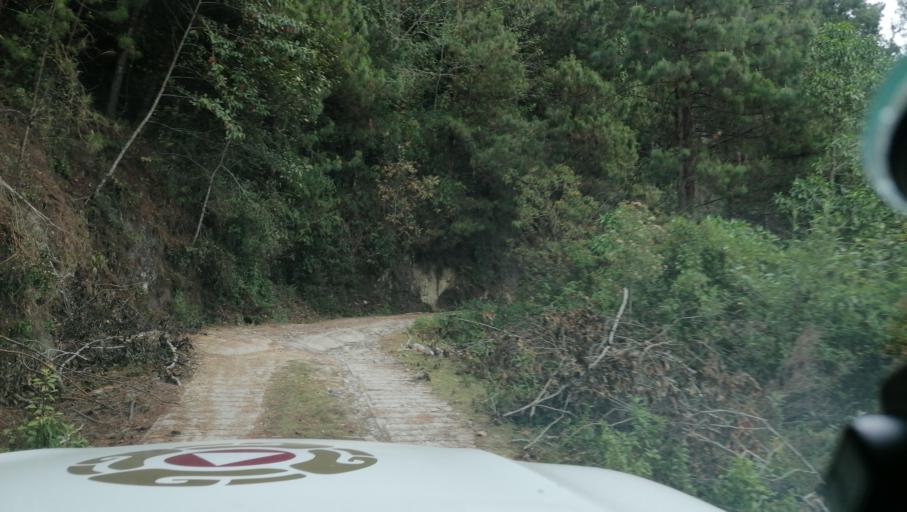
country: MX
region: Chiapas
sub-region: Tapachula
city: Canton Villaflor
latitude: 15.1972
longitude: -92.2329
